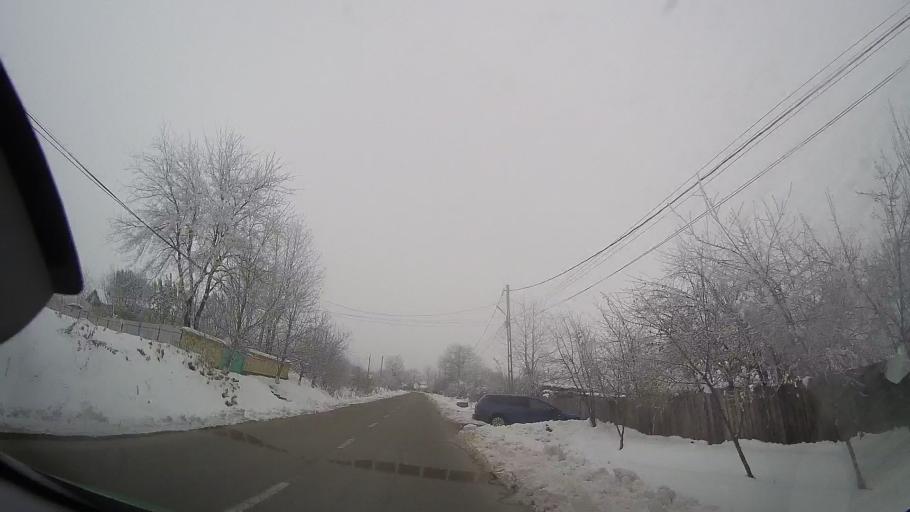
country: RO
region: Neamt
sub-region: Comuna Icusesti
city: Balusesti
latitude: 46.8620
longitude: 27.0056
